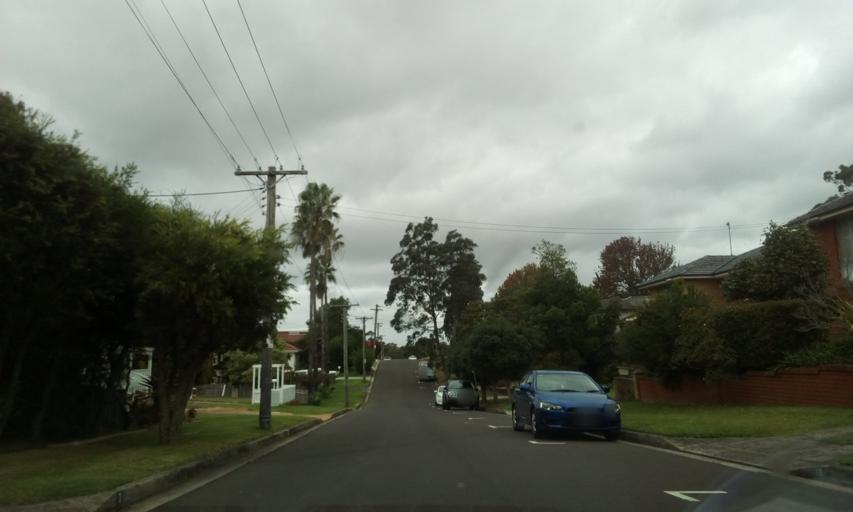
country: AU
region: New South Wales
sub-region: Wollongong
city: Mount Ousley
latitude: -34.4079
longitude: 150.8706
